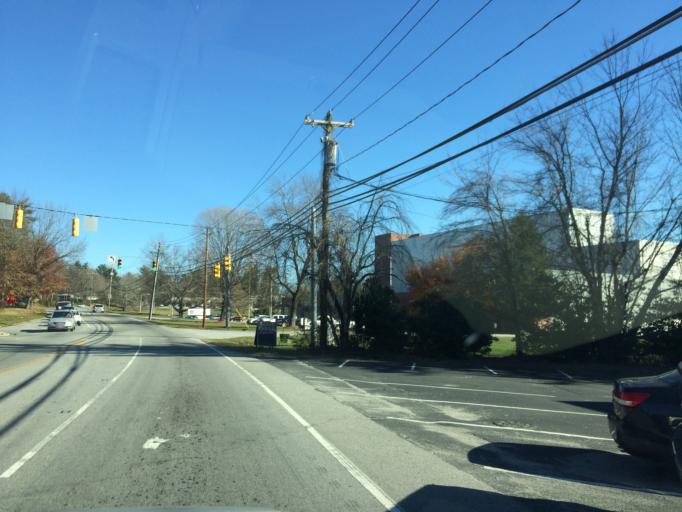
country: US
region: North Carolina
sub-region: Henderson County
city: Laurel Park
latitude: 35.3205
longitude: -82.4914
